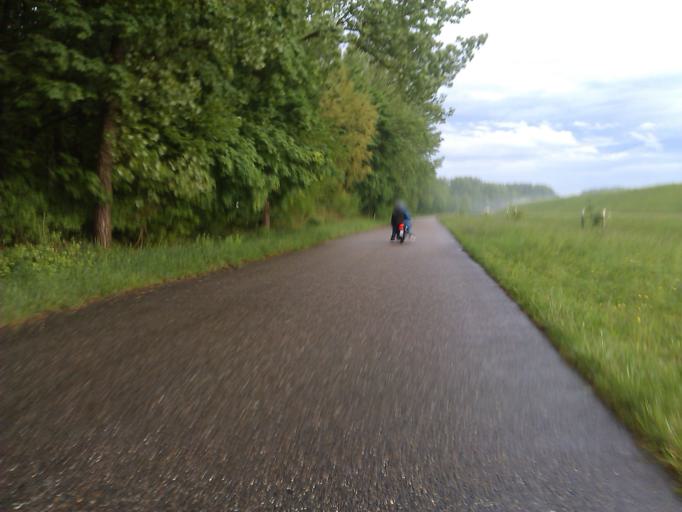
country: DE
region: Baden-Wuerttemberg
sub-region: Karlsruhe Region
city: Lichtenau
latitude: 48.7328
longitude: 7.9700
